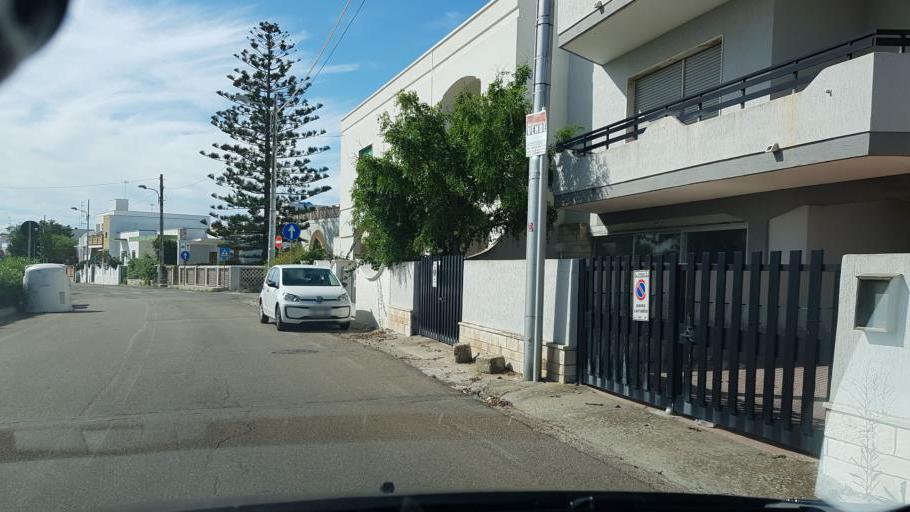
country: IT
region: Apulia
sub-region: Provincia di Lecce
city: Borgagne
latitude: 40.2769
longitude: 18.4292
